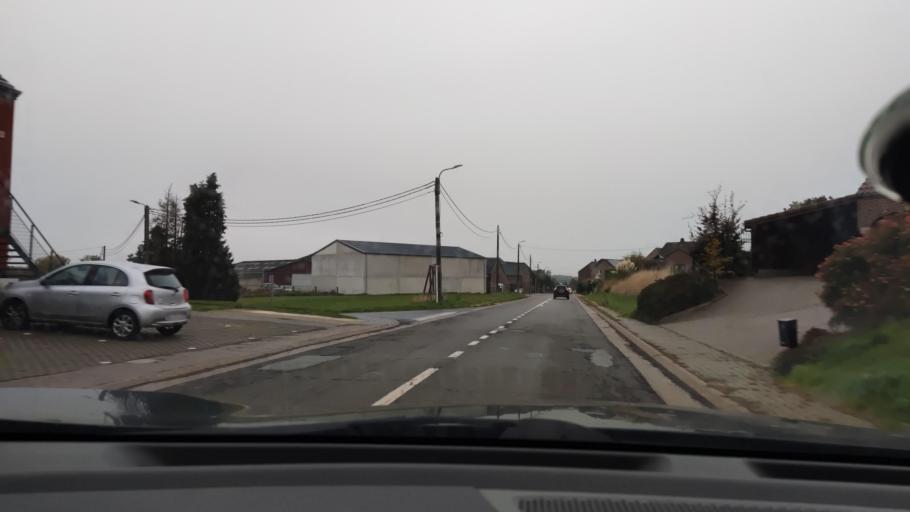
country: BE
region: Wallonia
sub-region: Province de Liege
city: Lincent
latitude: 50.7235
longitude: 4.9696
